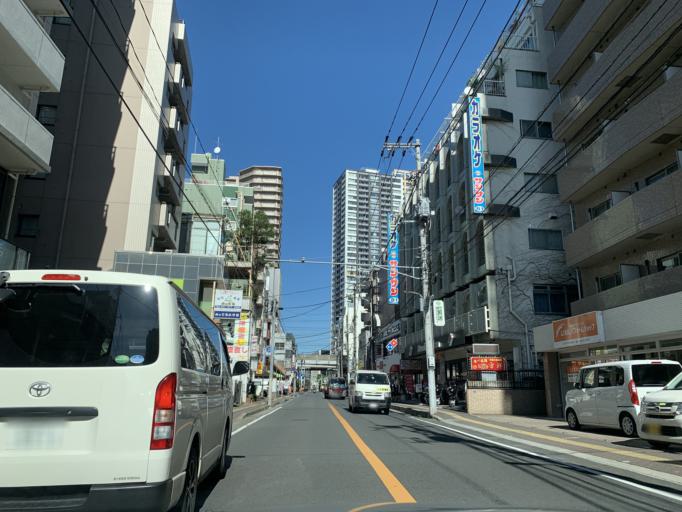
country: JP
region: Tokyo
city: Urayasu
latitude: 35.7205
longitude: 139.9250
